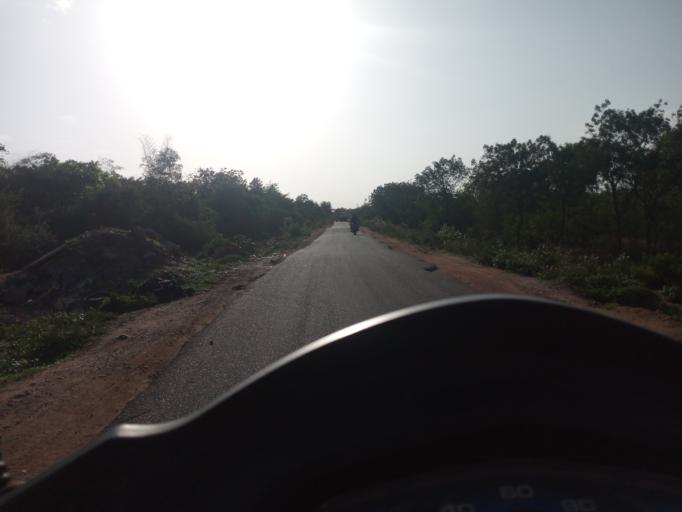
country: IN
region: Telangana
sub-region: Rangareddi
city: Quthbullapur
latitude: 17.5542
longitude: 78.4160
